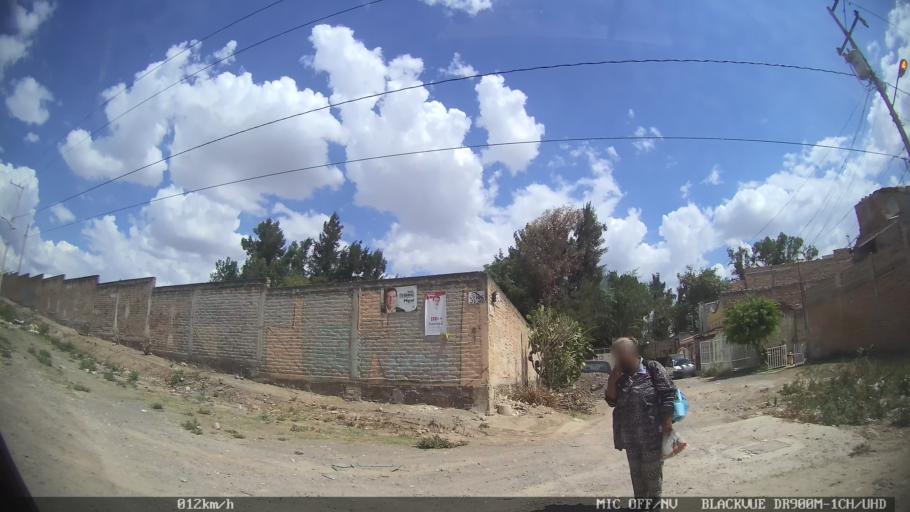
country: MX
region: Jalisco
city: Tlaquepaque
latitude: 20.6667
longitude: -103.2588
